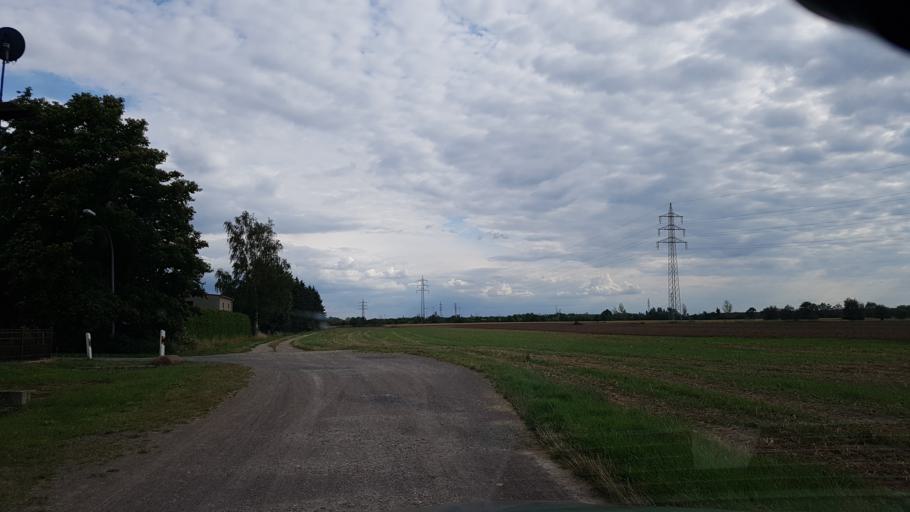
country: DE
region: Brandenburg
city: Falkenberg
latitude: 51.5789
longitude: 13.2269
